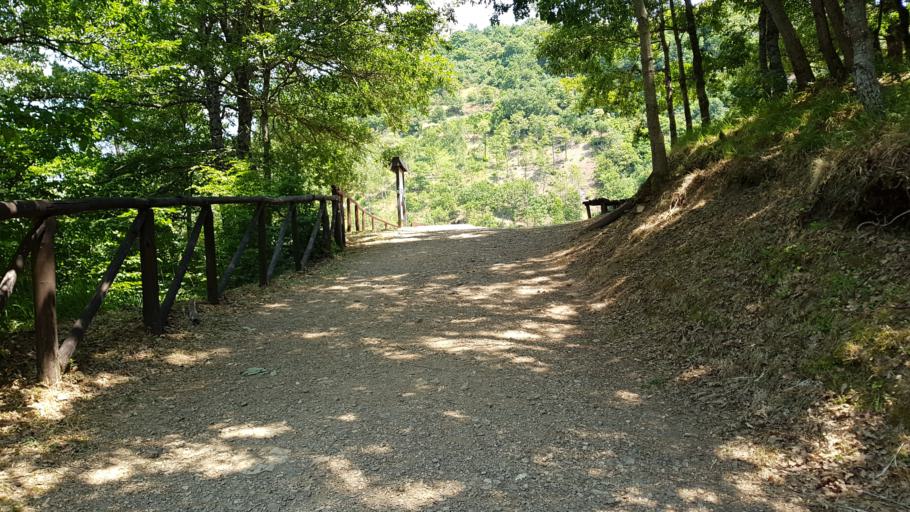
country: IT
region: Basilicate
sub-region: Provincia di Potenza
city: San Fele
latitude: 40.8152
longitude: 15.5291
